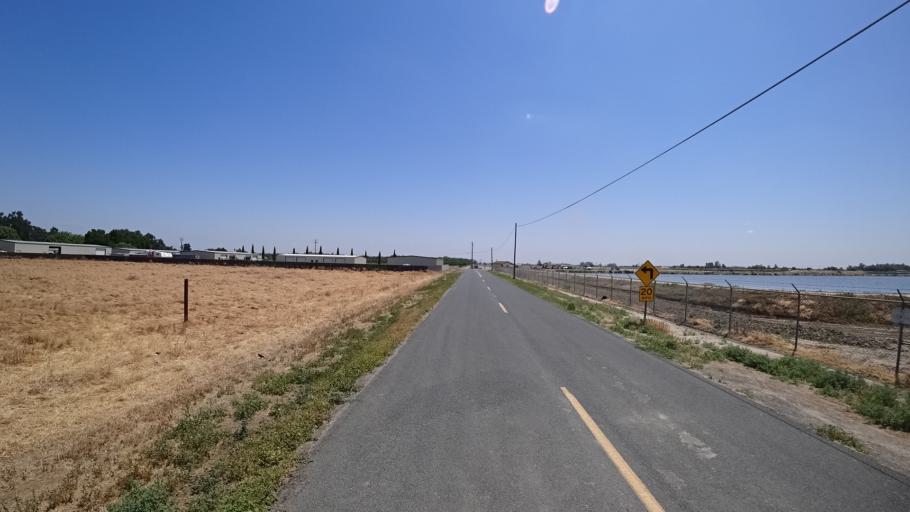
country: US
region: California
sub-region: Kings County
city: Armona
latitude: 36.3057
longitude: -119.7037
